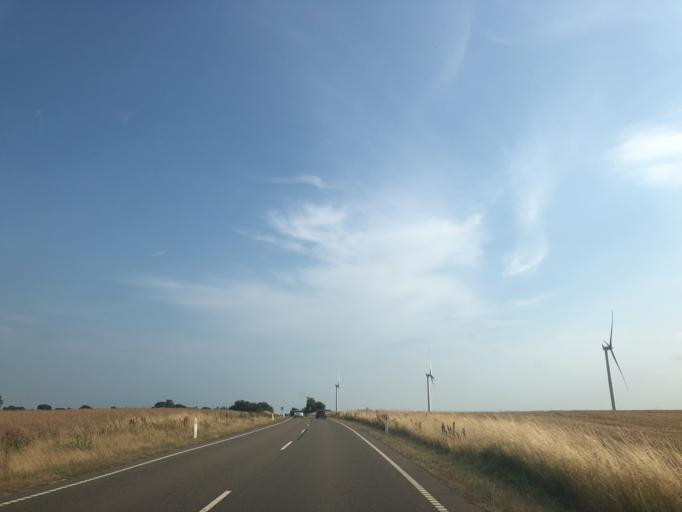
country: DK
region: North Denmark
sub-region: Morso Kommune
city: Nykobing Mors
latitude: 56.7715
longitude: 9.0358
